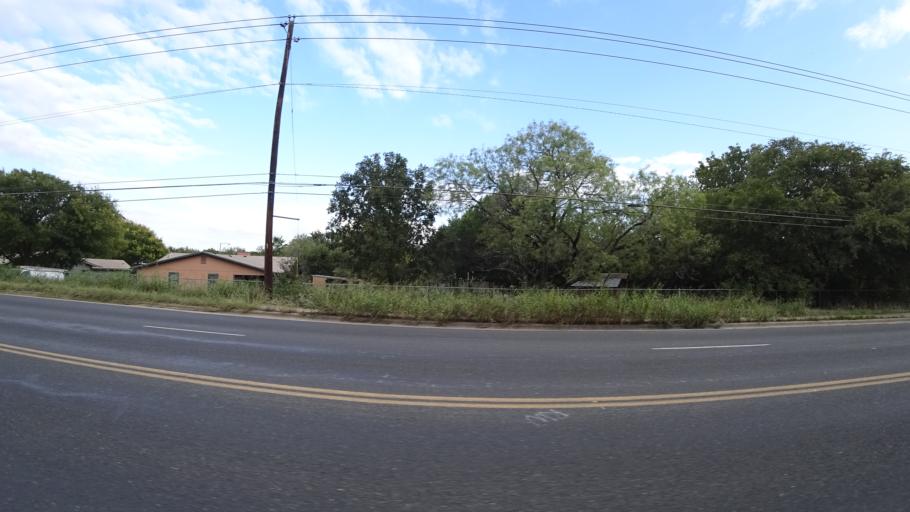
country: US
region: Texas
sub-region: Travis County
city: Onion Creek
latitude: 30.1862
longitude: -97.7910
